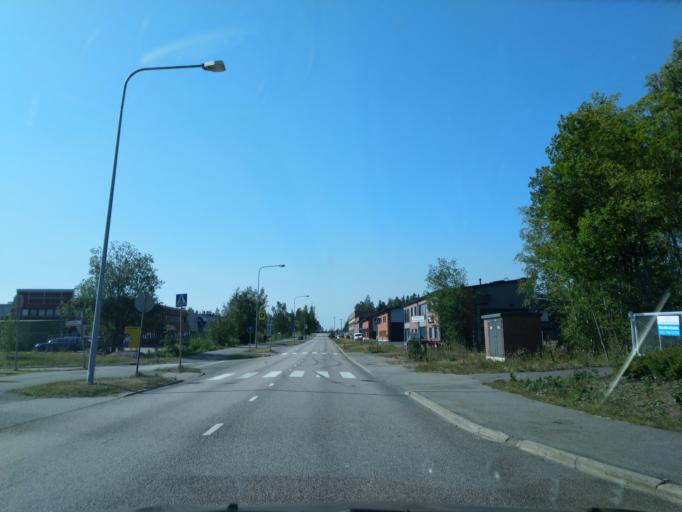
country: FI
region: Uusimaa
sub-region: Helsinki
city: Kauniainen
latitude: 60.2604
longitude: 24.7199
